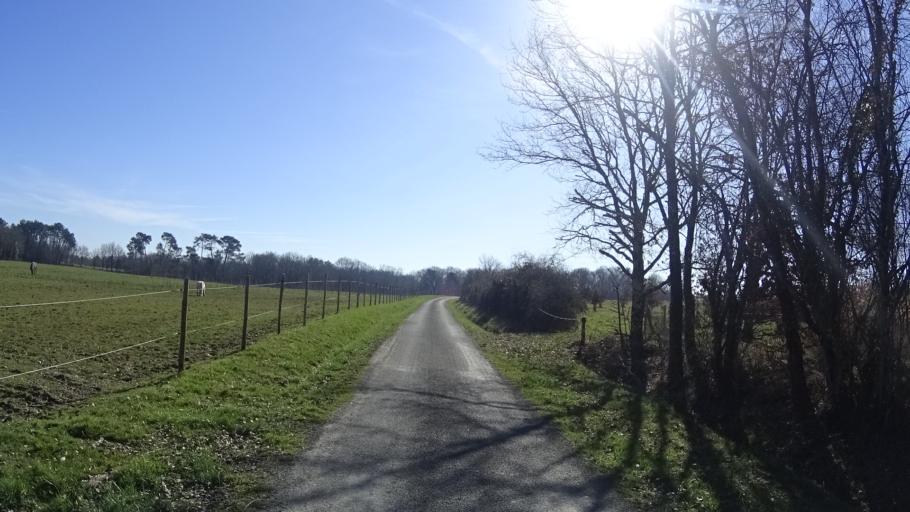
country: FR
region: Aquitaine
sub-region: Departement de la Dordogne
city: Saint-Aulaye
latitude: 45.1321
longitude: 0.2227
